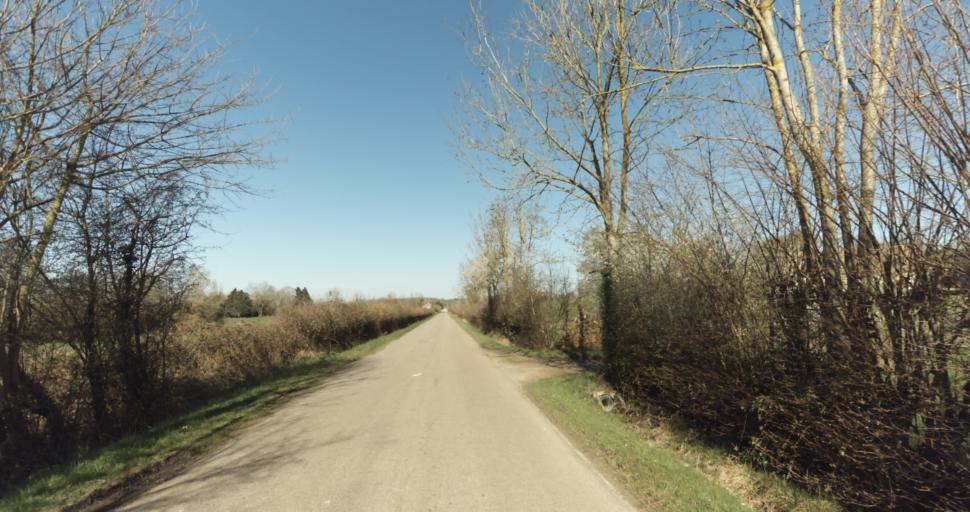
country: FR
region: Lower Normandy
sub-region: Departement du Calvados
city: Saint-Pierre-sur-Dives
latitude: 48.9714
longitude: 0.0464
